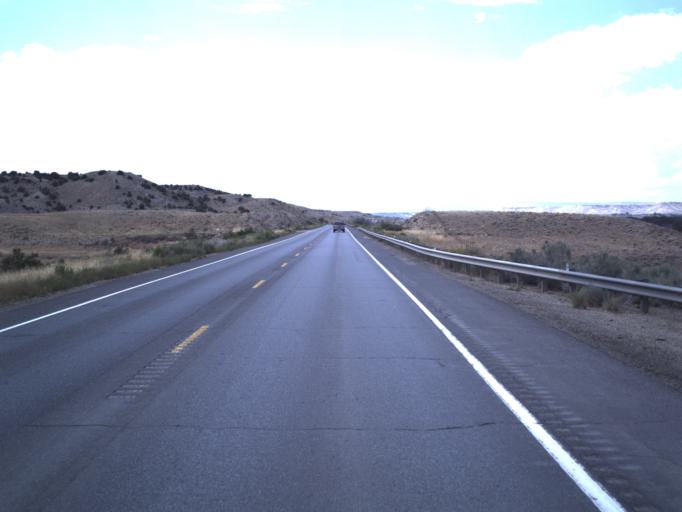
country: US
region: Utah
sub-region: Duchesne County
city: Duchesne
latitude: 40.1579
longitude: -110.2592
